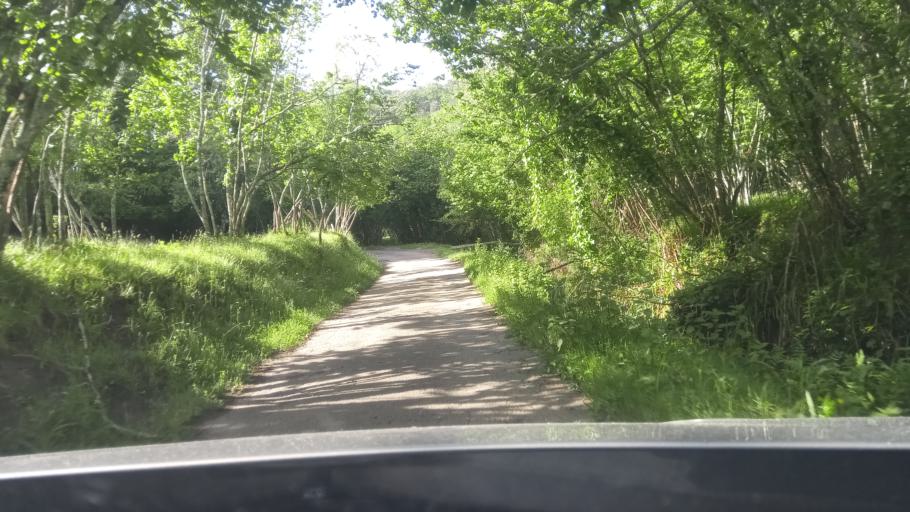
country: IT
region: Latium
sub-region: Provincia di Latina
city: Minturno
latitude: 41.2776
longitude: 13.7657
